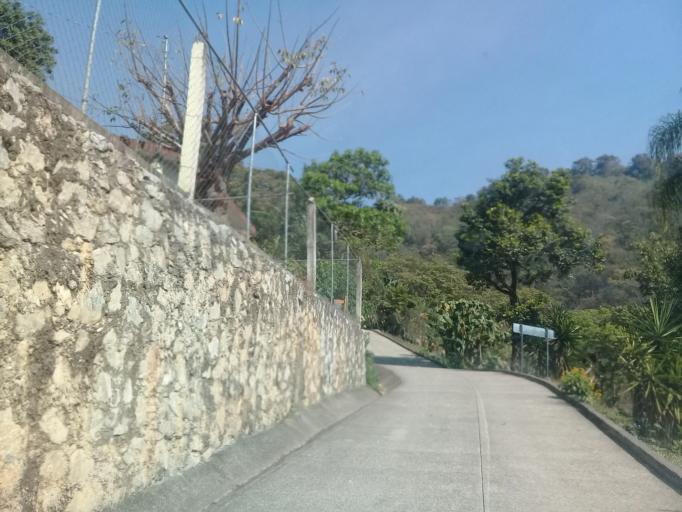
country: MX
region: Veracruz
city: Rafael Delgado
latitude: 18.7836
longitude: -97.0278
